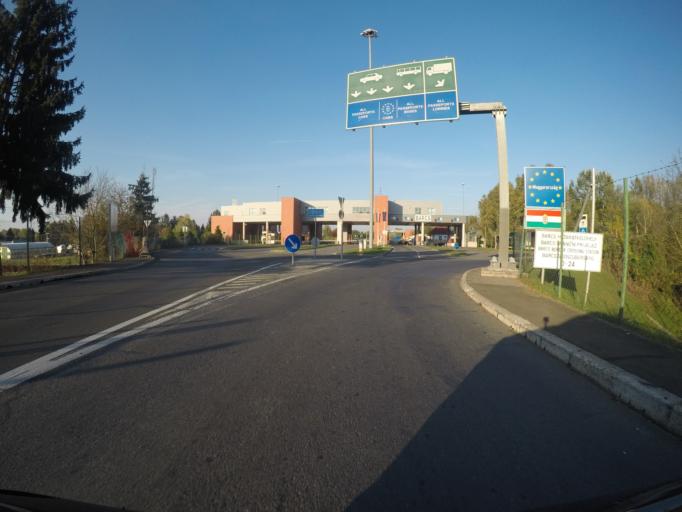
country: HU
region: Somogy
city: Barcs
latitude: 45.9470
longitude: 17.4622
